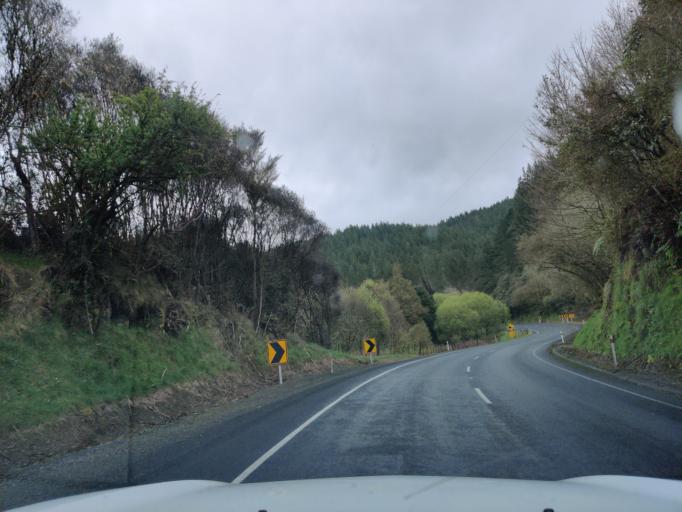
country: NZ
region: Waikato
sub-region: Otorohanga District
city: Otorohanga
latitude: -38.6582
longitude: 175.2081
